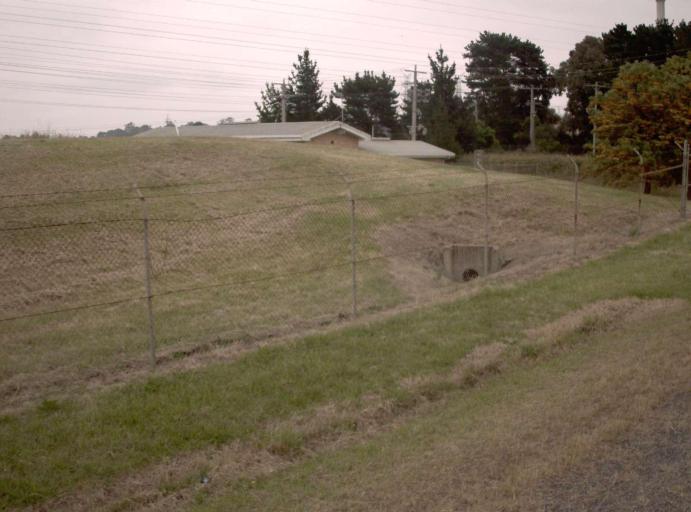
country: AU
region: Victoria
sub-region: Latrobe
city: Morwell
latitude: -38.2763
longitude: 146.3975
